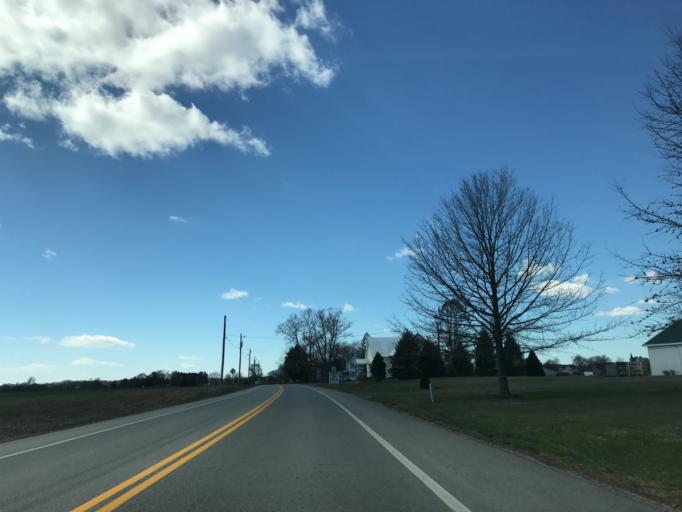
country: US
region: Maryland
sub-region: Caroline County
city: Greensboro
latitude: 39.0926
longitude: -75.8702
